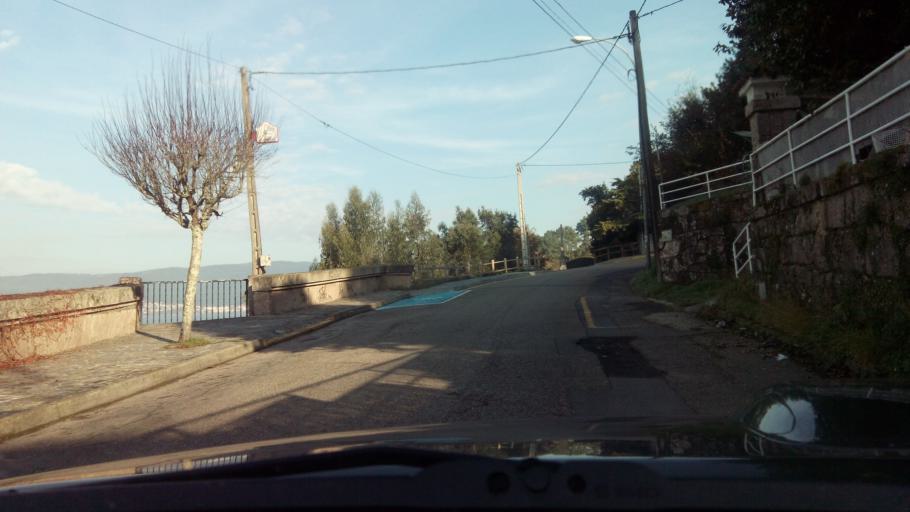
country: ES
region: Galicia
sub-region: Provincia de Pontevedra
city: Marin
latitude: 42.3757
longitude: -8.7290
